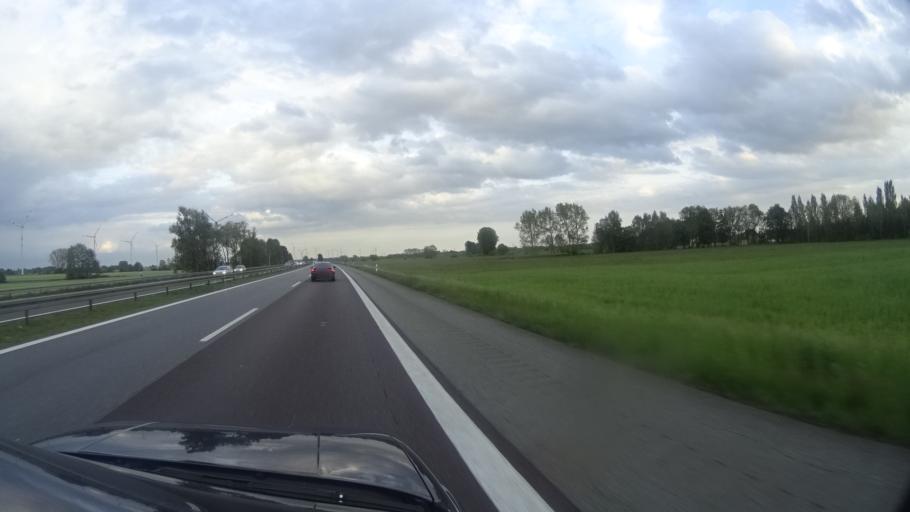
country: DE
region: Brandenburg
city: Walsleben
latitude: 52.9418
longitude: 12.6752
